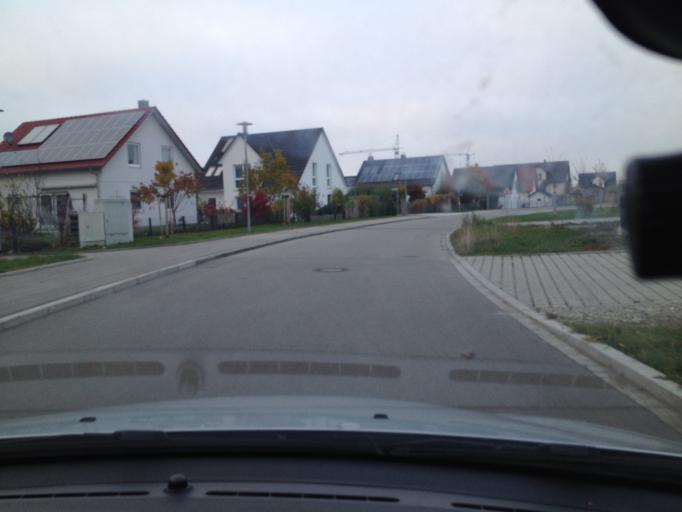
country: DE
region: Bavaria
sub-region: Swabia
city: Kleinaitingen
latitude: 48.2192
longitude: 10.8469
